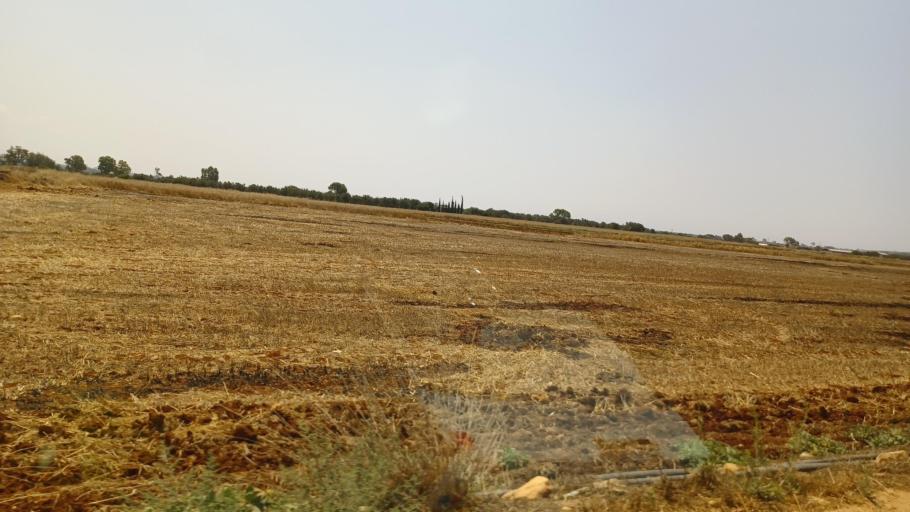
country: CY
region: Ammochostos
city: Liopetri
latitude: 34.9814
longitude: 33.8665
